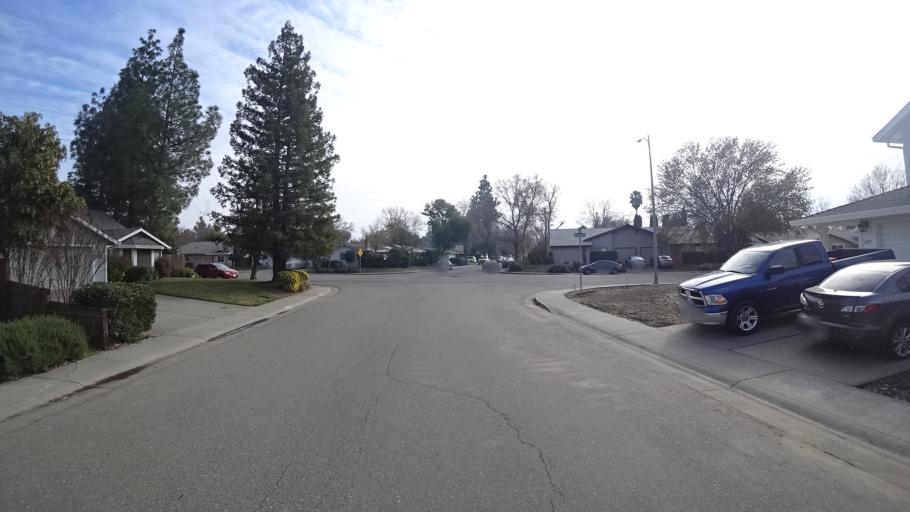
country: US
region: California
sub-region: Yolo County
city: Davis
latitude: 38.5465
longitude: -121.7162
